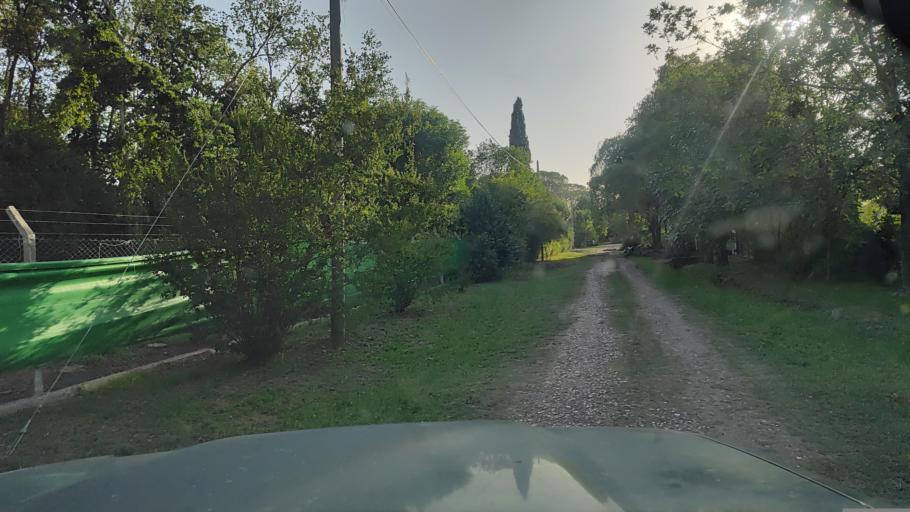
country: AR
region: Buenos Aires
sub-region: Partido de Lujan
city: Lujan
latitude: -34.5477
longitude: -59.1901
